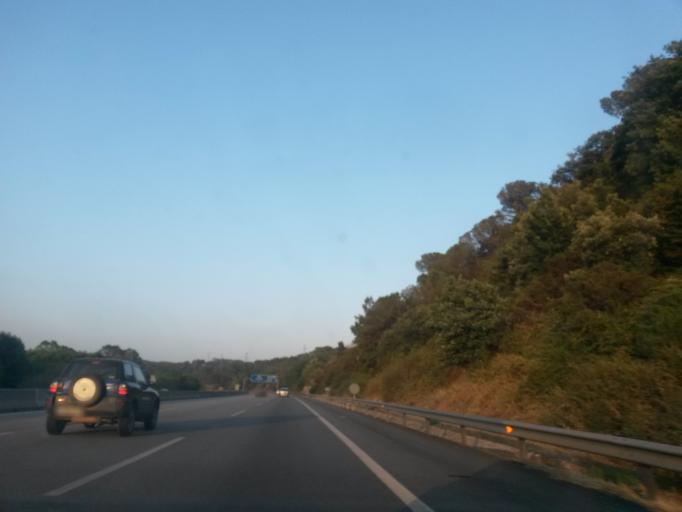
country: ES
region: Catalonia
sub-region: Provincia de Girona
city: Hostalric
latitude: 41.7291
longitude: 2.6237
